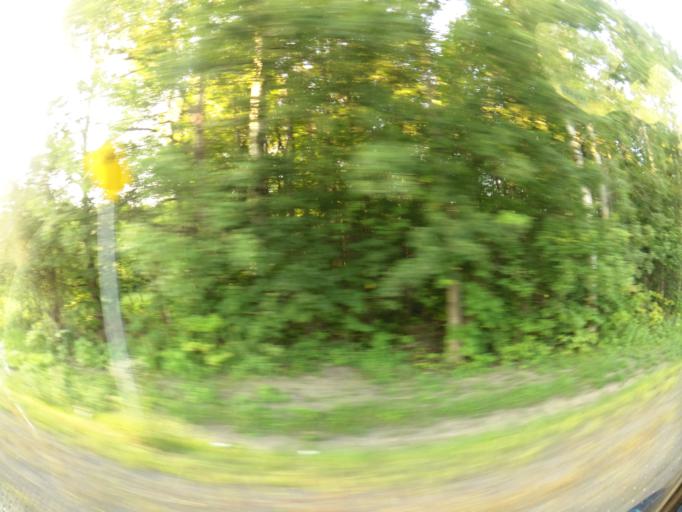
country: CA
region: Ontario
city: Clarence-Rockland
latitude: 45.4987
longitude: -75.4368
